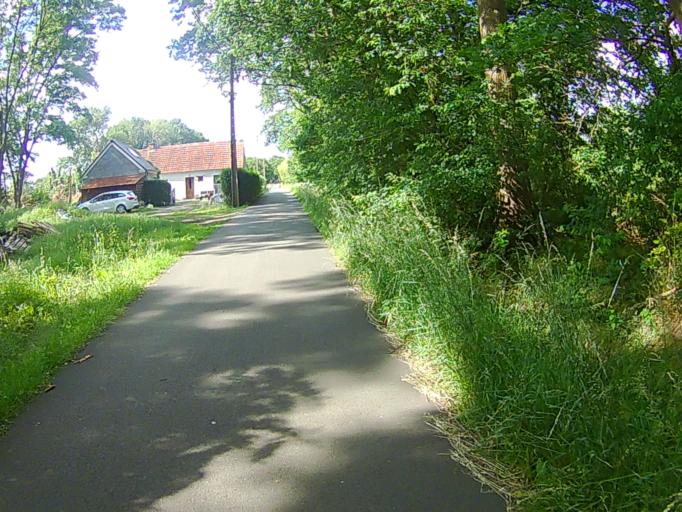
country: BE
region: Flanders
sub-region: Provincie Antwerpen
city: Berlaar
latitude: 51.1122
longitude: 4.6968
